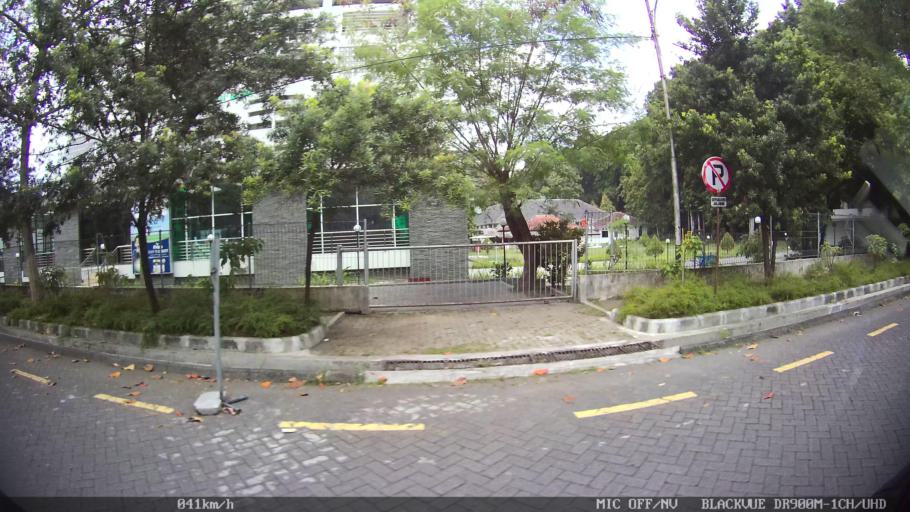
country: ID
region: Daerah Istimewa Yogyakarta
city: Yogyakarta
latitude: -7.7652
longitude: 110.3765
